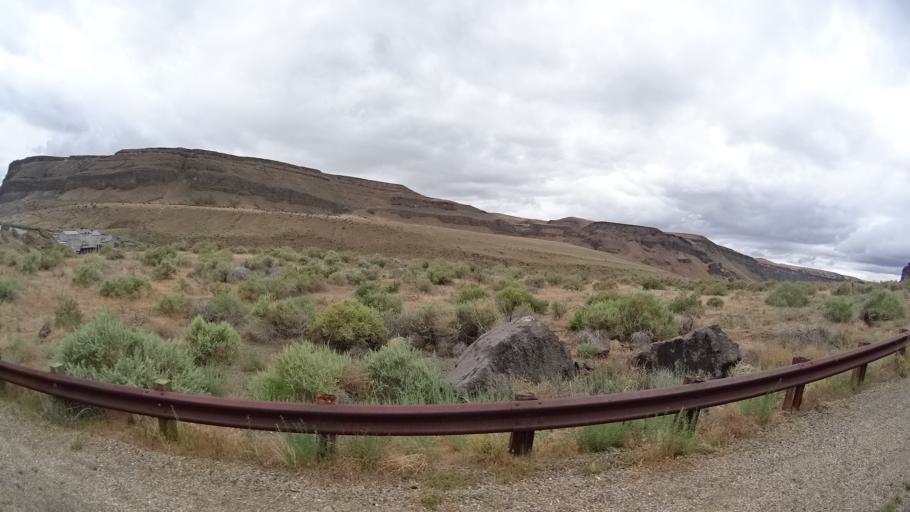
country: US
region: Idaho
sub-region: Owyhee County
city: Murphy
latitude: 43.2478
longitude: -116.3760
